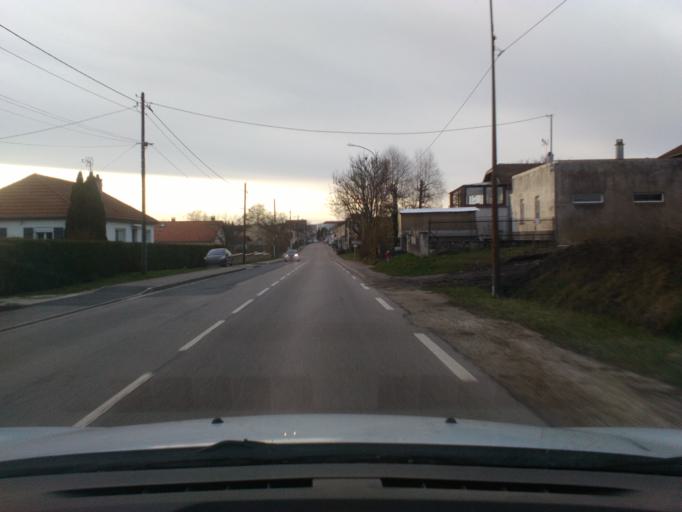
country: FR
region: Lorraine
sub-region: Departement des Vosges
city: Charmes
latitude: 48.3744
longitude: 6.3039
